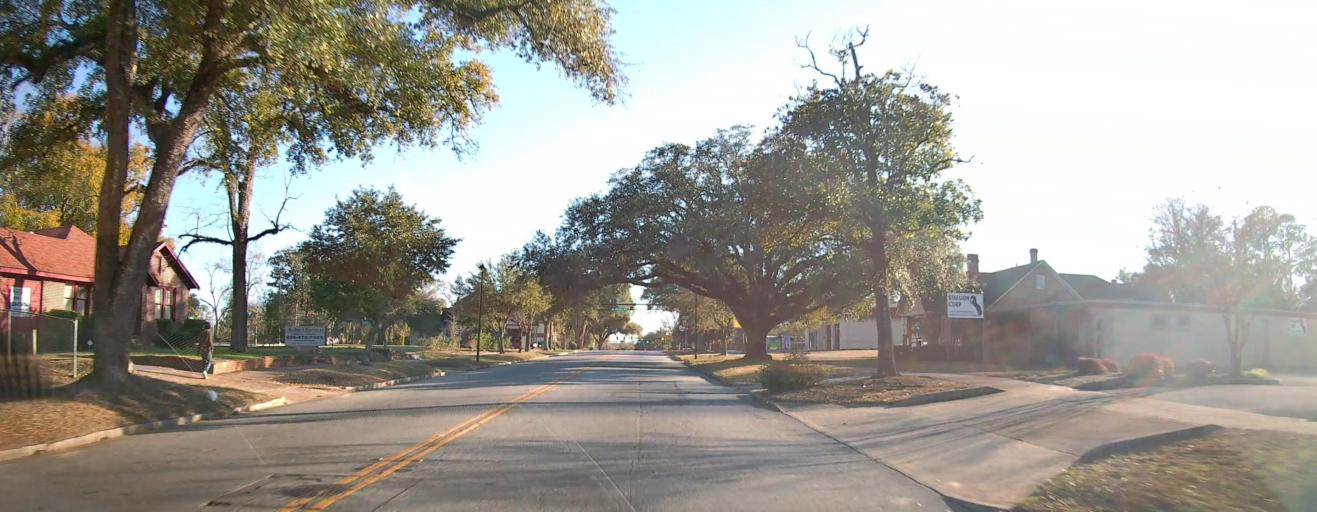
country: US
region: Georgia
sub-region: Dougherty County
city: Albany
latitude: 31.5872
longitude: -84.1561
